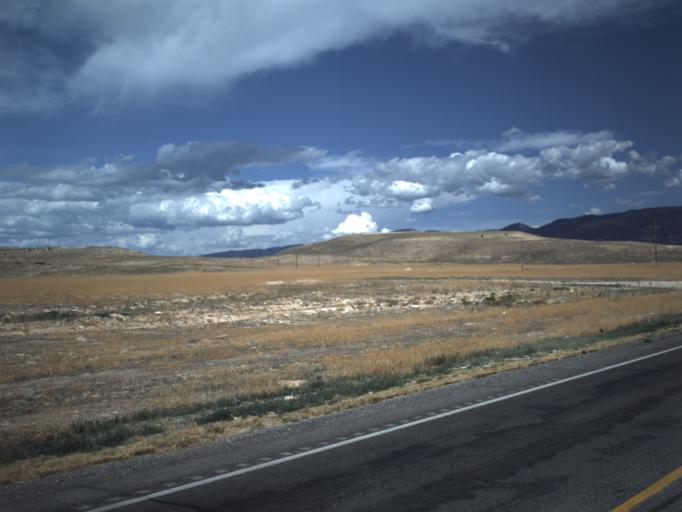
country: US
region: Utah
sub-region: Sanpete County
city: Gunnison
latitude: 39.1611
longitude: -111.7894
